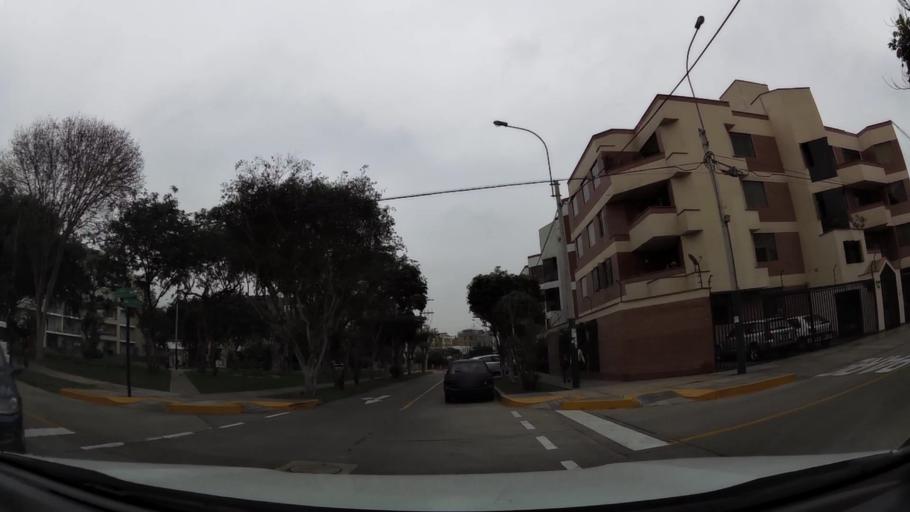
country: PE
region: Lima
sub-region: Lima
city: Surco
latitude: -12.1319
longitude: -77.0054
